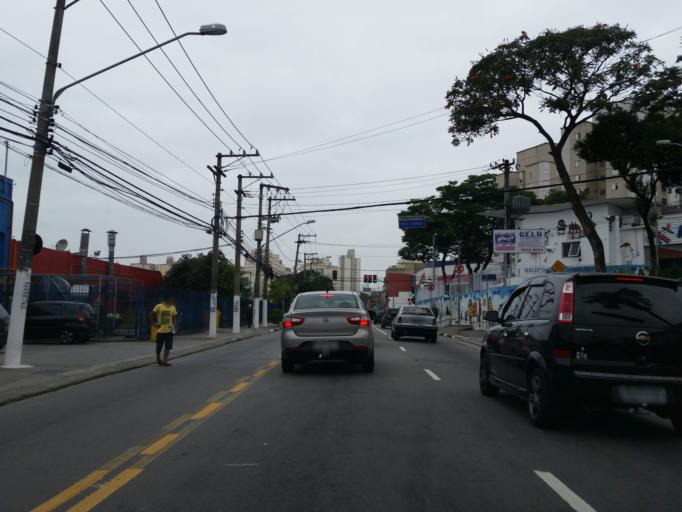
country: BR
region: Sao Paulo
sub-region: Diadema
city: Diadema
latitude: -23.6642
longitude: -46.6802
